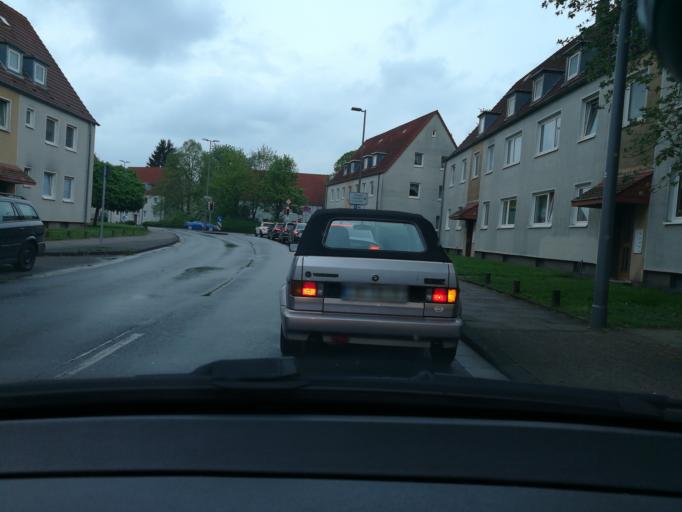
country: DE
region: North Rhine-Westphalia
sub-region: Regierungsbezirk Detmold
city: Herford
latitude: 52.1062
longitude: 8.6830
